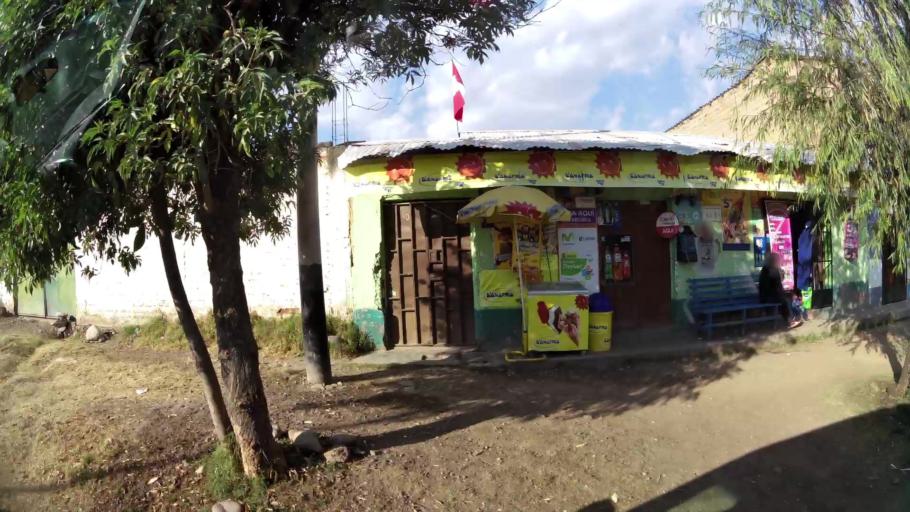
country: PE
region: Junin
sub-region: Provincia de Huancayo
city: El Tambo
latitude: -12.0454
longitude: -75.2169
